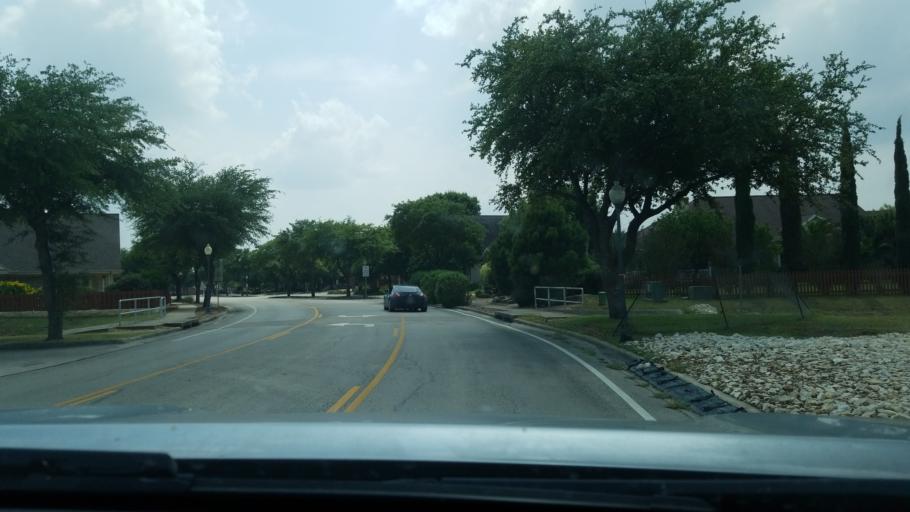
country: US
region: Texas
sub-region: Comal County
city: New Braunfels
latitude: 29.7301
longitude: -98.0982
